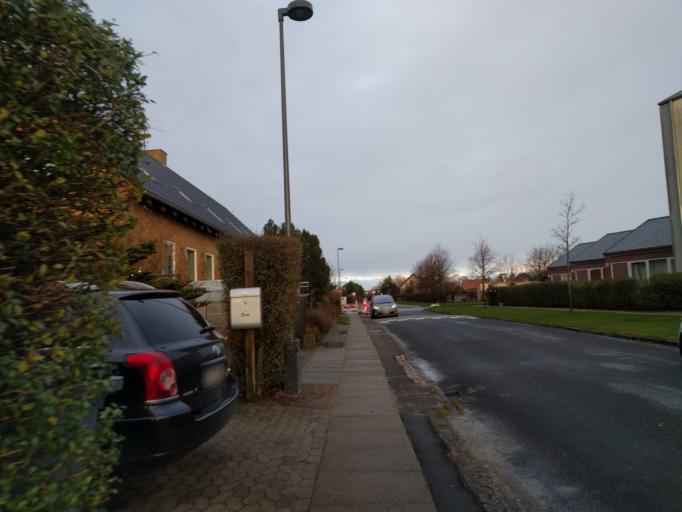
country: DK
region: Capital Region
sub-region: Tarnby Kommune
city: Tarnby
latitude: 55.6470
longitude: 12.6328
